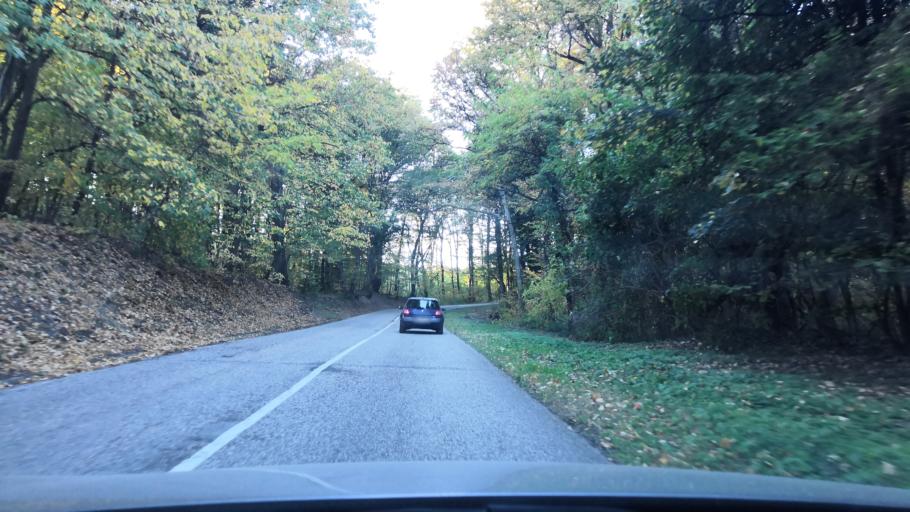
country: RS
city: Vrdnik
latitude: 45.1513
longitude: 19.7763
